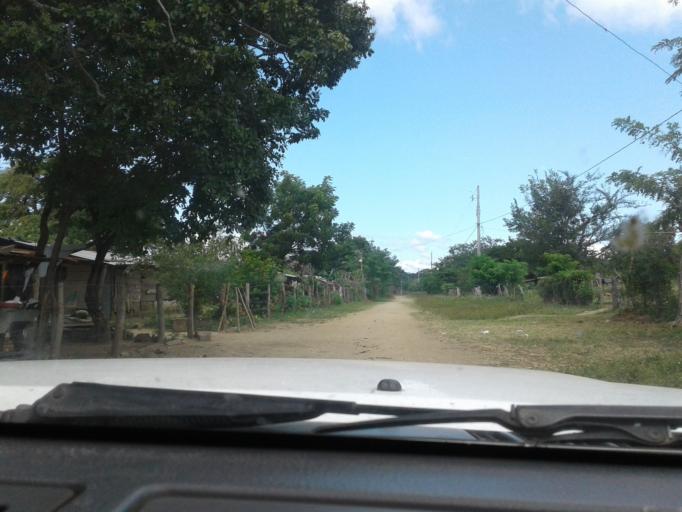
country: NI
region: Rivas
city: Belen
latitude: 11.6334
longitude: -85.9539
